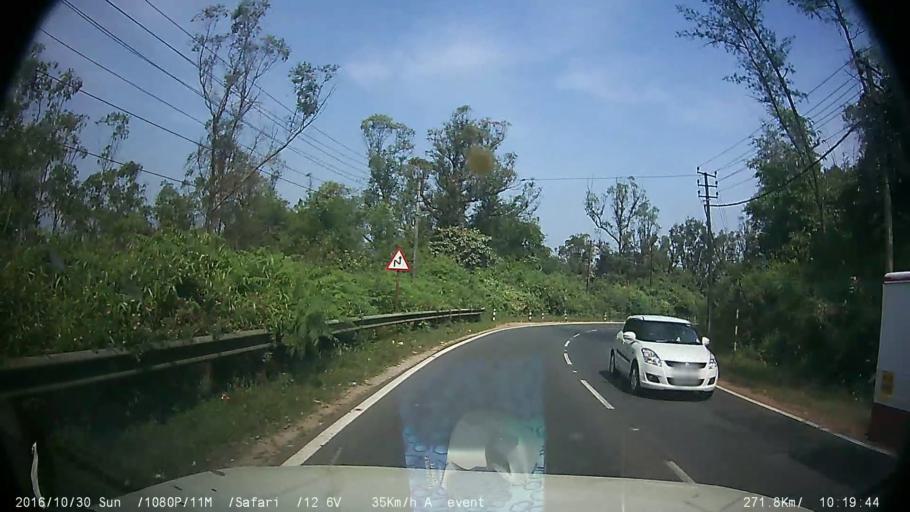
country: IN
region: Karnataka
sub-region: Kodagu
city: Madikeri
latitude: 12.4270
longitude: 75.7530
